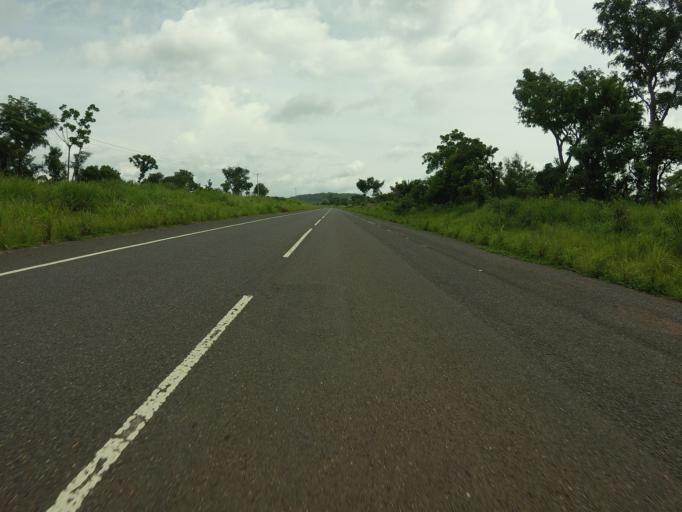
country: TG
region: Plateaux
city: Badou
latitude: 7.9596
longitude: 0.5557
